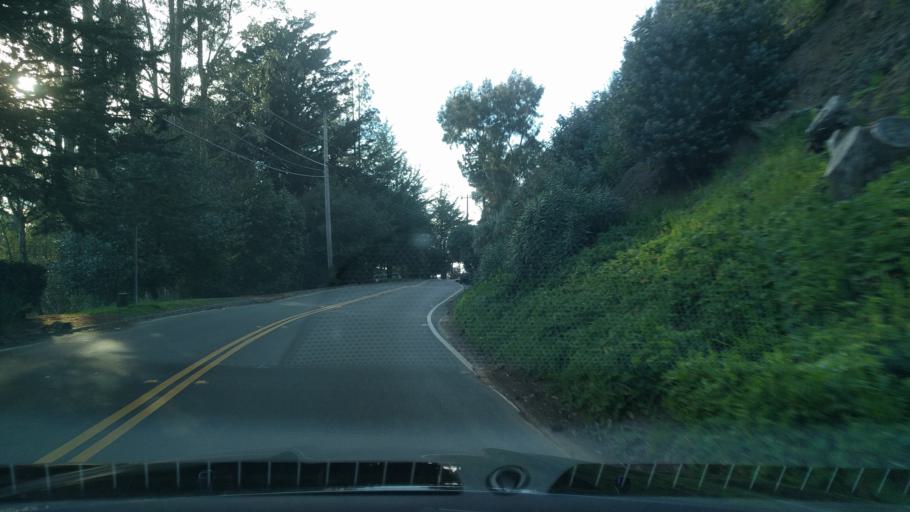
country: US
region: California
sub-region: Alameda County
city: Piedmont
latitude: 37.8397
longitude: -122.1954
